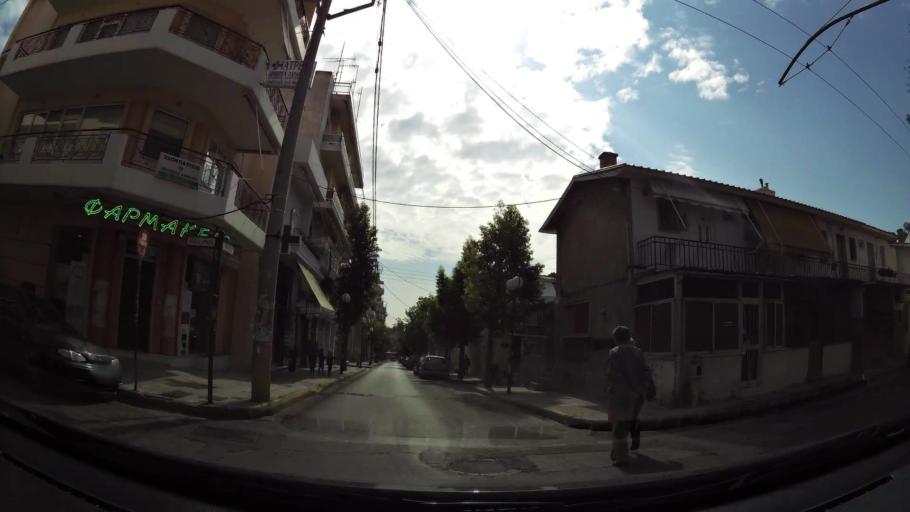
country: GR
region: Attica
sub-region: Nomos Piraios
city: Keratsini
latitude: 37.9615
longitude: 23.6260
